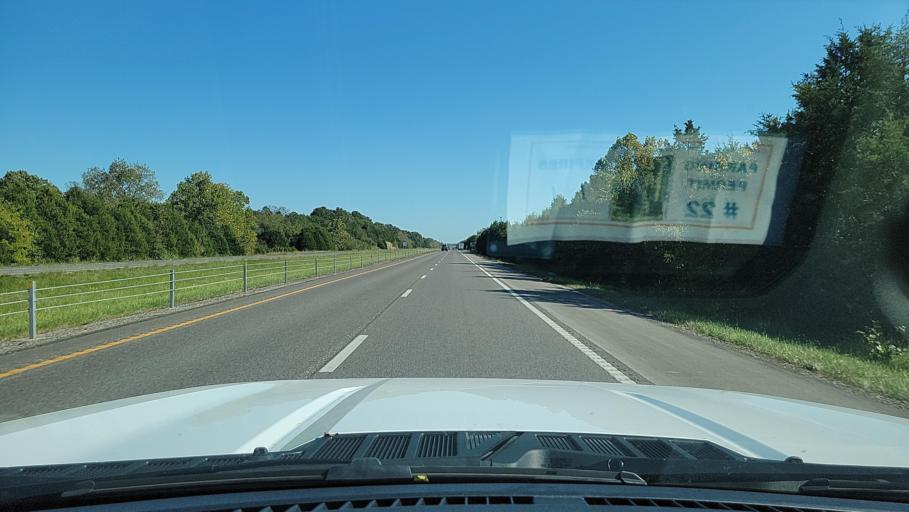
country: US
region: Missouri
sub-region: Sainte Genevieve County
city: Sainte Genevieve
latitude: 37.9671
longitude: -90.1816
